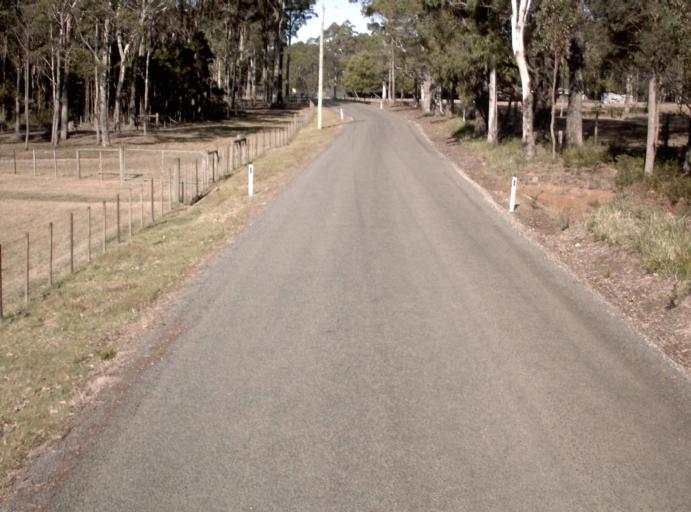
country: AU
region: Tasmania
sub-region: Launceston
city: Mayfield
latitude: -41.3138
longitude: 147.2014
